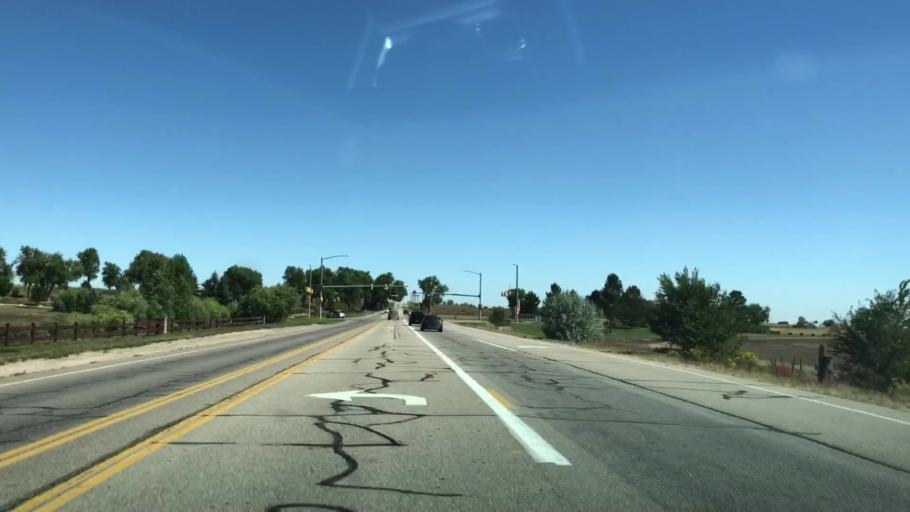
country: US
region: Colorado
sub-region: Weld County
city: Windsor
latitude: 40.5229
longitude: -104.9567
